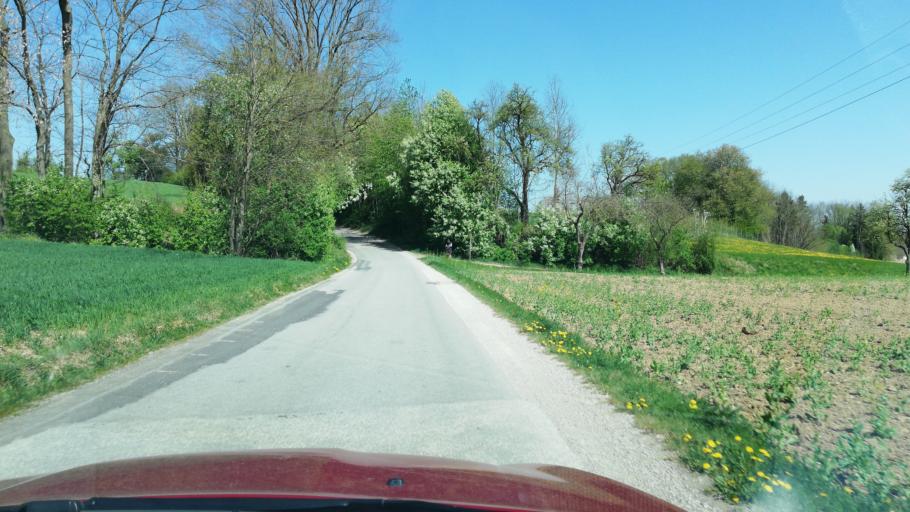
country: AT
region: Upper Austria
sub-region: Politischer Bezirk Kirchdorf an der Krems
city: Kremsmunster
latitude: 48.0471
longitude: 14.1561
